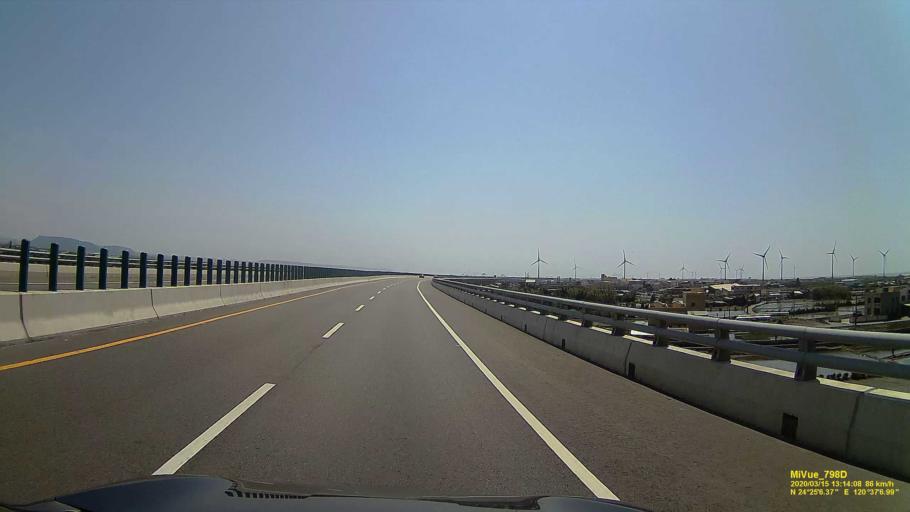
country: TW
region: Taiwan
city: Fengyuan
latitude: 24.4179
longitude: 120.6185
